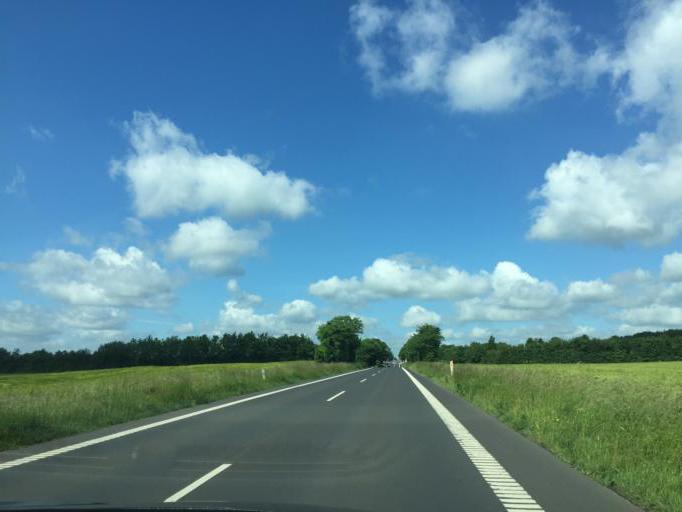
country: DK
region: South Denmark
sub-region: Fredericia Kommune
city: Taulov
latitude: 55.5317
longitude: 9.6474
